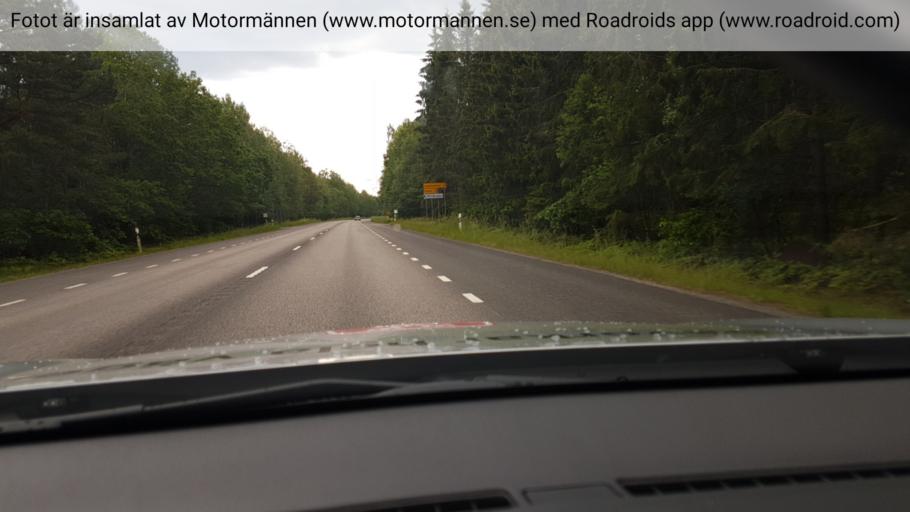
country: SE
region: Vaestra Goetaland
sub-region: Hjo Kommun
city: Hjo
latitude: 58.2747
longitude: 14.2615
